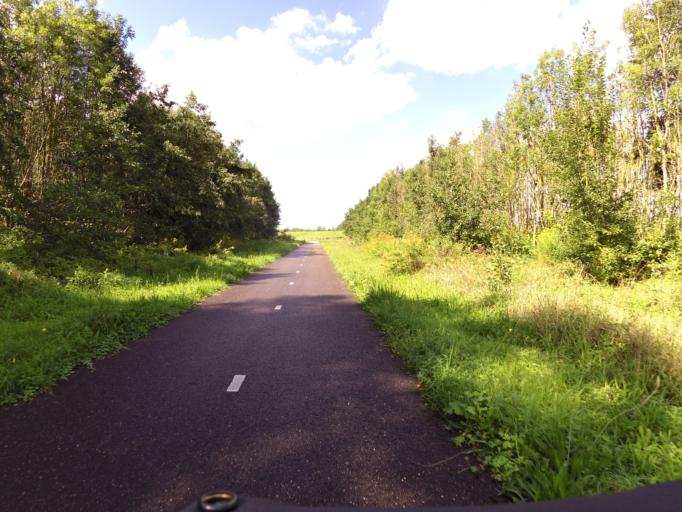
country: NL
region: North Brabant
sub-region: Gemeente Steenbergen
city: Dinteloord
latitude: 51.7040
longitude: 4.3189
